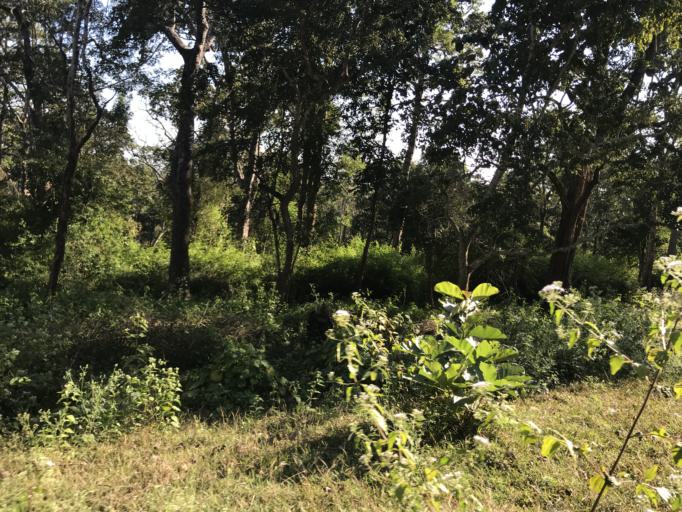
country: IN
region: Karnataka
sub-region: Mysore
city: Heggadadevankote
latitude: 11.9582
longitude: 76.2342
